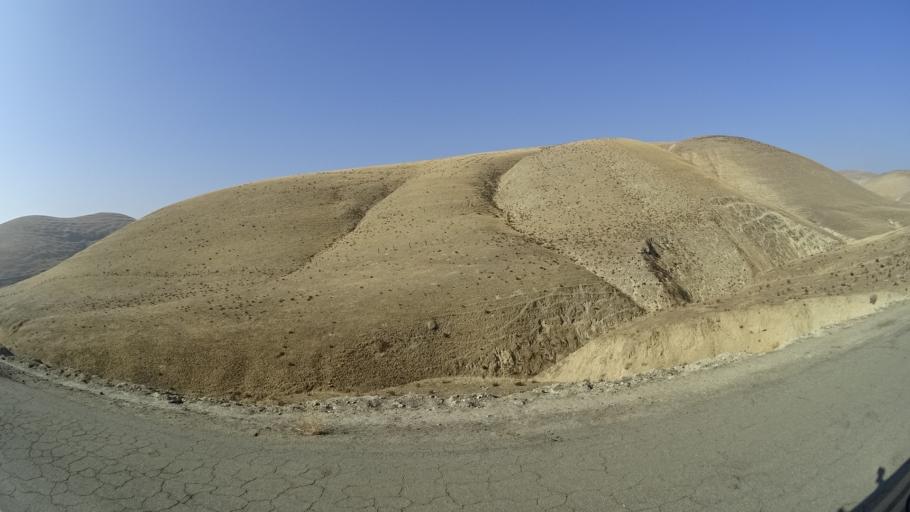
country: US
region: California
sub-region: Kern County
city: Oildale
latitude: 35.4519
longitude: -118.8275
